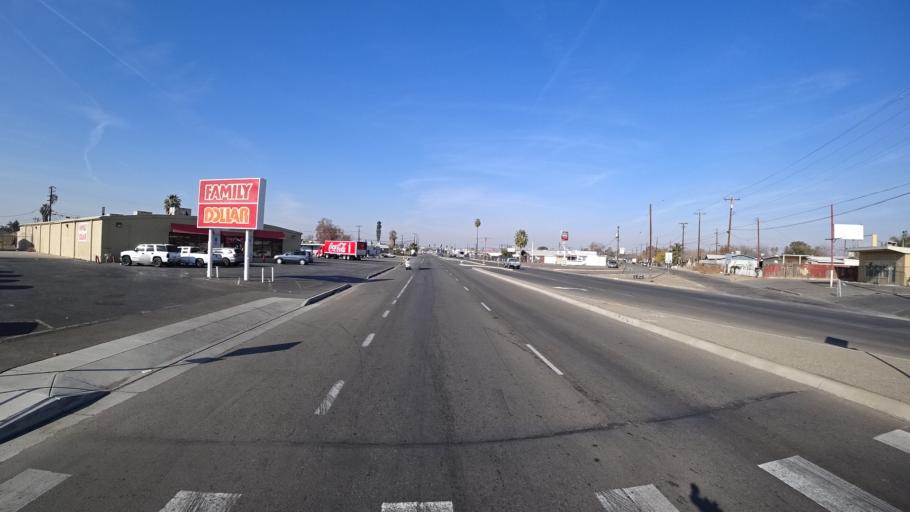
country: US
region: California
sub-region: Kern County
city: Bakersfield
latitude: 35.3340
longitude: -119.0153
